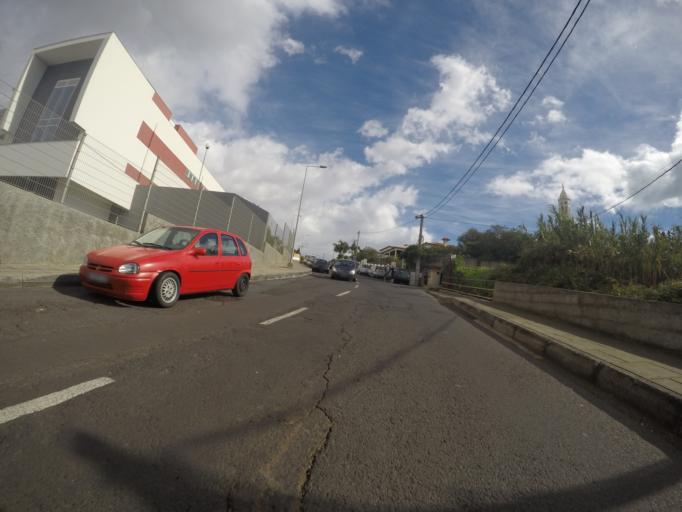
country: PT
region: Madeira
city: Camara de Lobos
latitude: 32.6505
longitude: -16.9452
